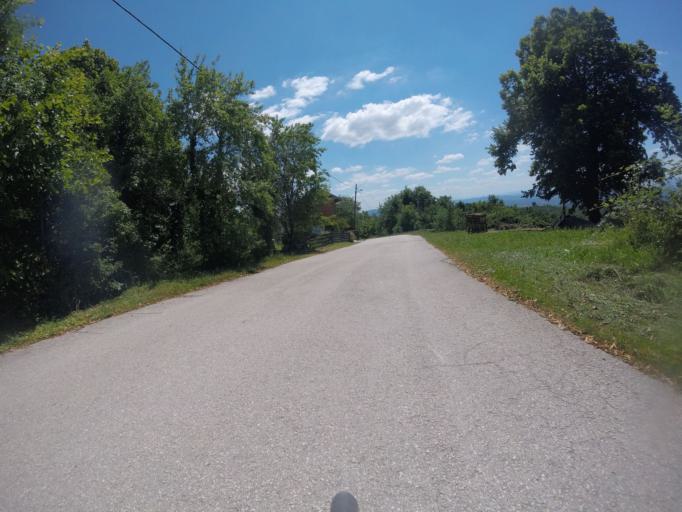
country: SI
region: Metlika
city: Metlika
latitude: 45.7070
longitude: 15.3873
